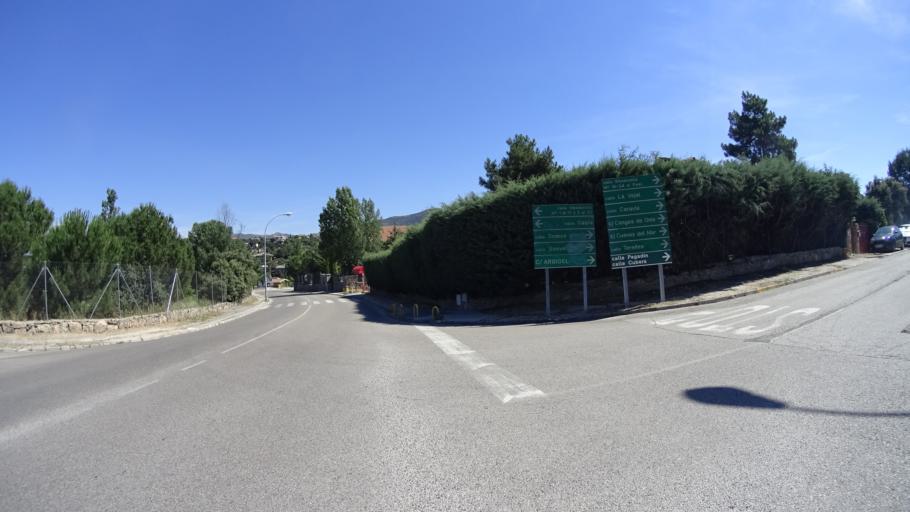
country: ES
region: Madrid
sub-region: Provincia de Madrid
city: Torrelodones
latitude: 40.6027
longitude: -3.9401
